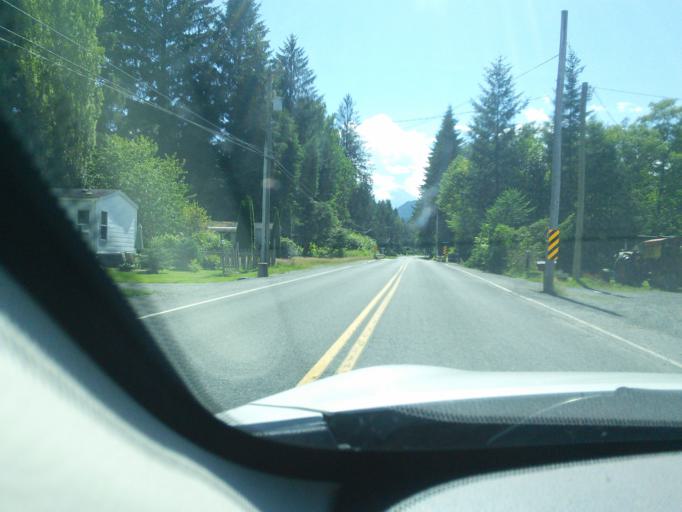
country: CA
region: British Columbia
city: Campbell River
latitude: 50.3381
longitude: -125.9101
